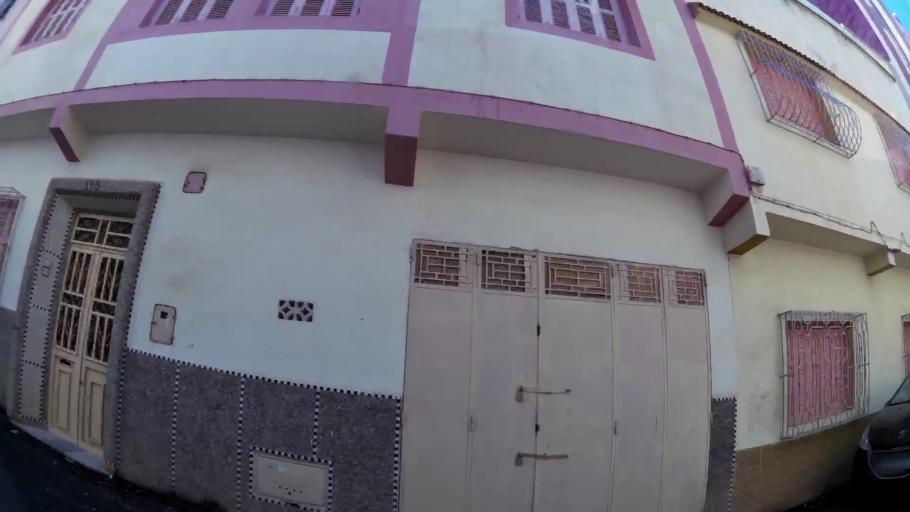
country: MA
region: Meknes-Tafilalet
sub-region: Meknes
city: Meknes
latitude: 33.8971
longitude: -5.5813
